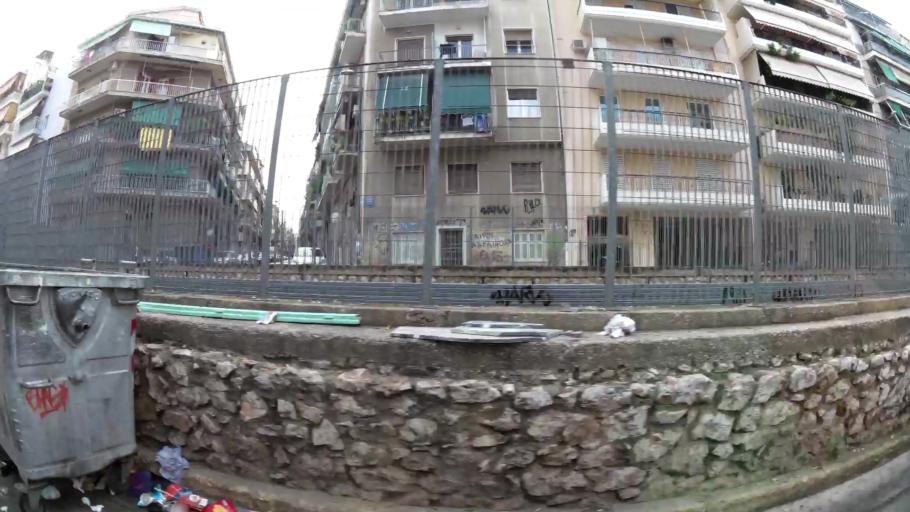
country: GR
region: Attica
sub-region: Nomarchia Athinas
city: Kipseli
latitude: 38.0023
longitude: 23.7240
